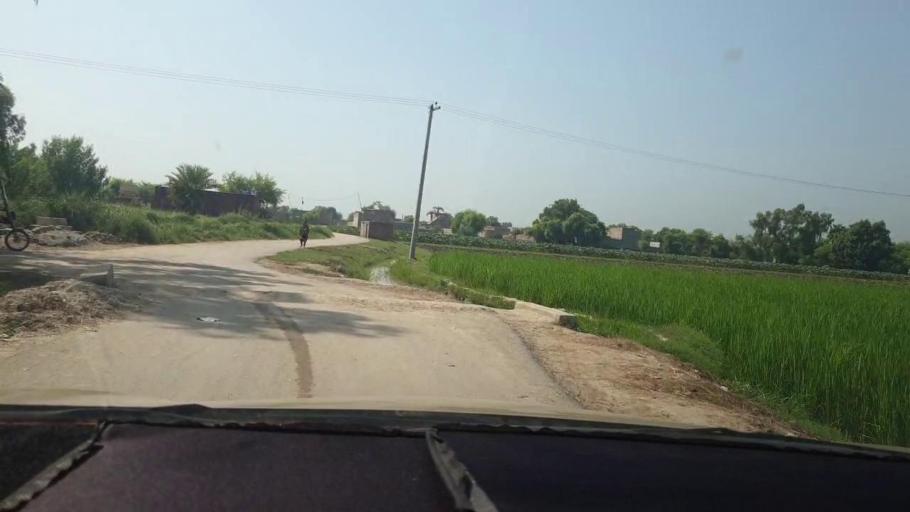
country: PK
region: Sindh
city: Kambar
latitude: 27.5552
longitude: 68.0407
